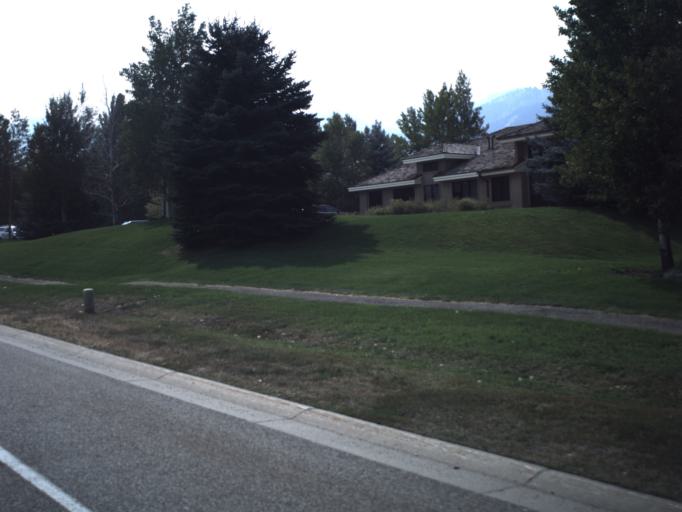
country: US
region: Utah
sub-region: Summit County
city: Snyderville
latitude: 40.6934
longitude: -111.5443
